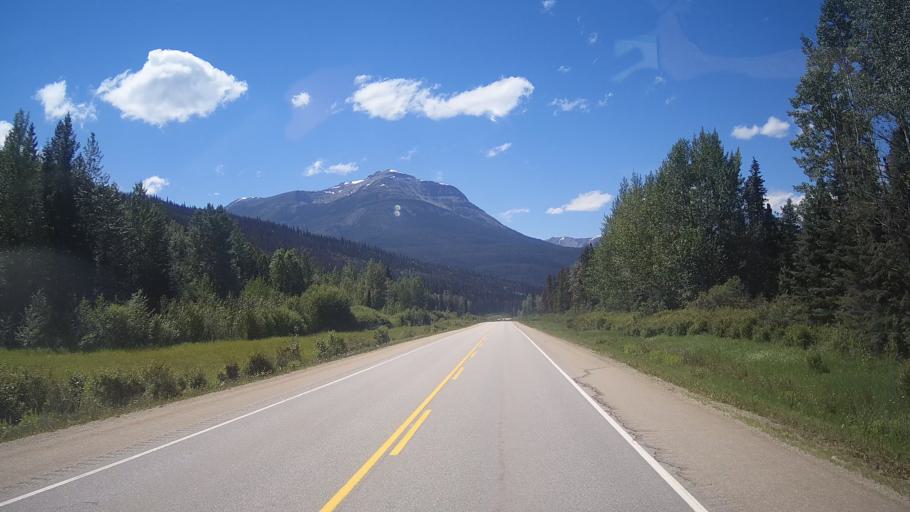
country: CA
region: Alberta
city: Jasper Park Lodge
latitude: 52.8527
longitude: -118.5556
